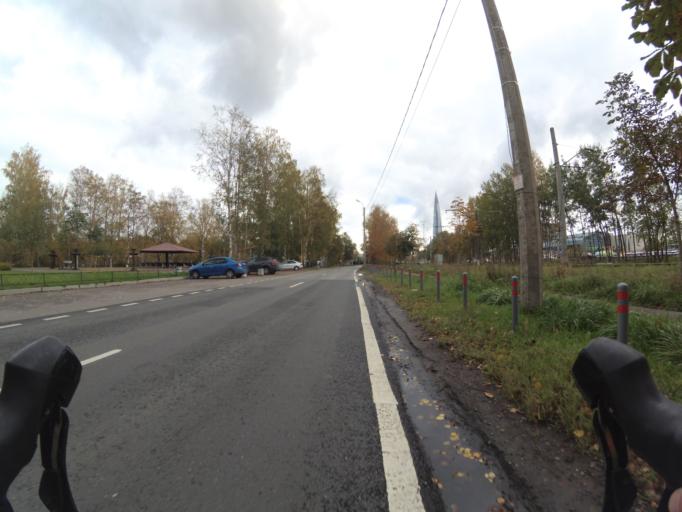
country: RU
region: St.-Petersburg
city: Lakhtinskiy
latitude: 59.9955
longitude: 30.1484
